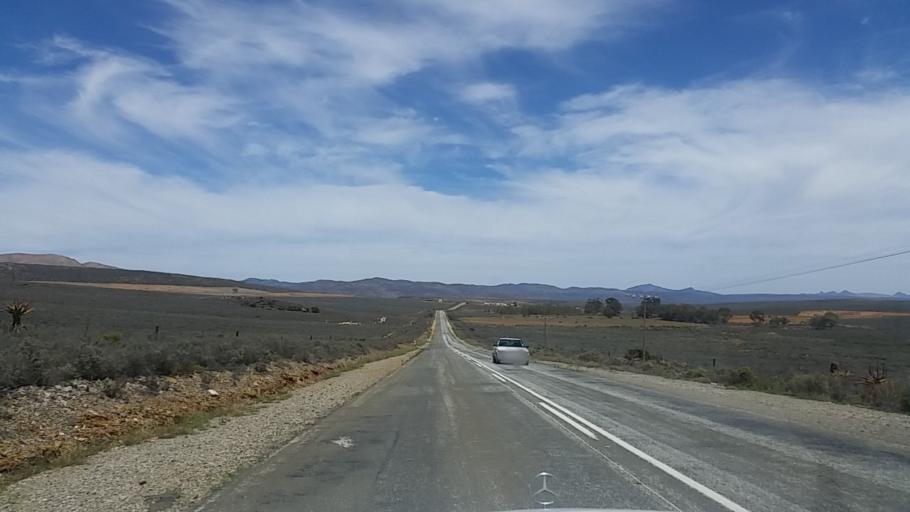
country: ZA
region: Eastern Cape
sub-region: Cacadu District Municipality
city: Willowmore
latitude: -33.5932
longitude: 23.1520
